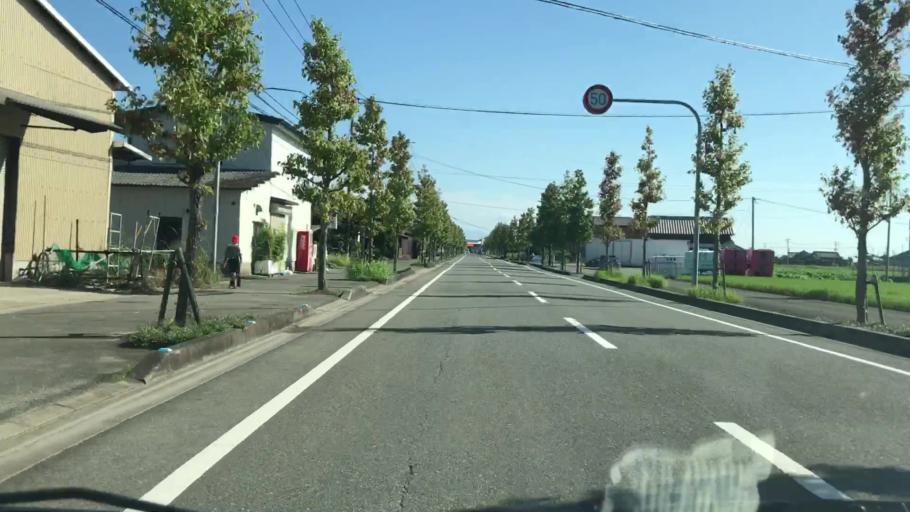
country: JP
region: Saga Prefecture
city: Okawa
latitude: 33.1860
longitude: 130.3138
